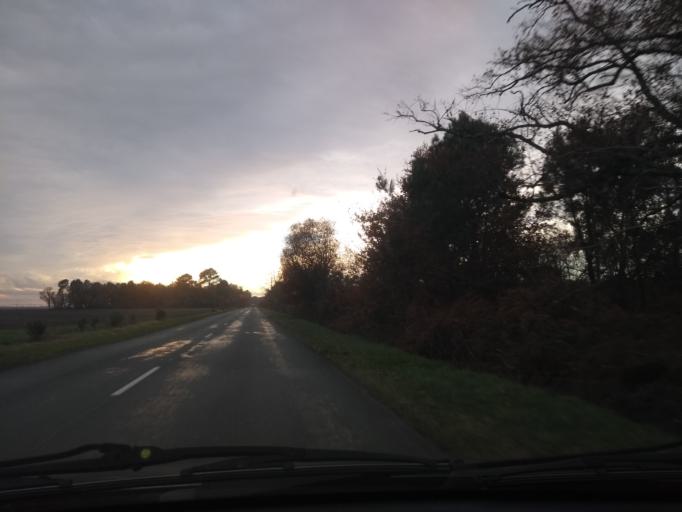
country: FR
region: Aquitaine
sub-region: Departement de la Gironde
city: Saucats
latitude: 44.6409
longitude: -0.6372
